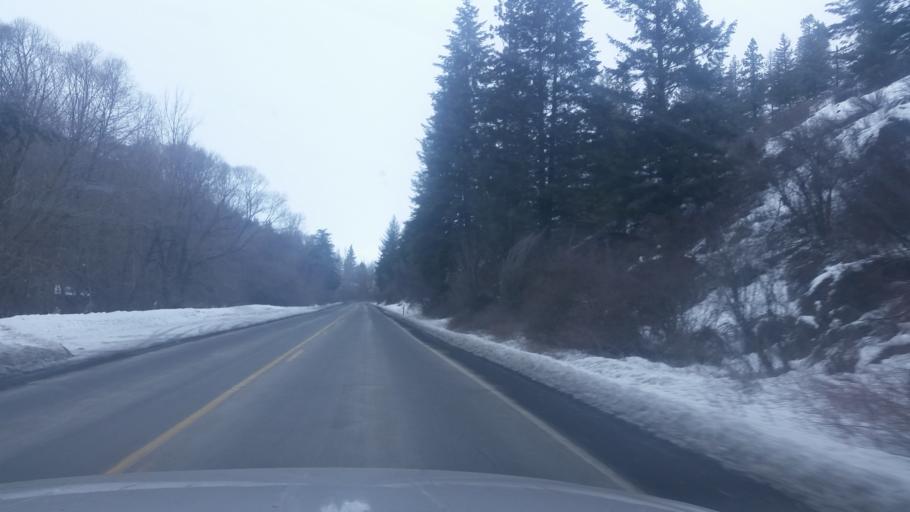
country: US
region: Washington
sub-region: Lincoln County
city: Davenport
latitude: 47.7638
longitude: -117.8909
